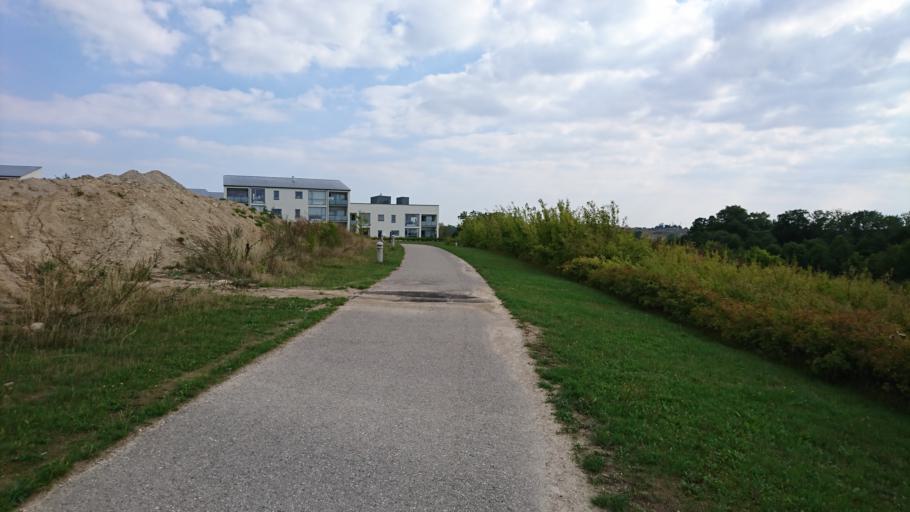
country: DK
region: Capital Region
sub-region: Egedal Kommune
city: Smorumnedre
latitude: 55.7465
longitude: 12.2857
